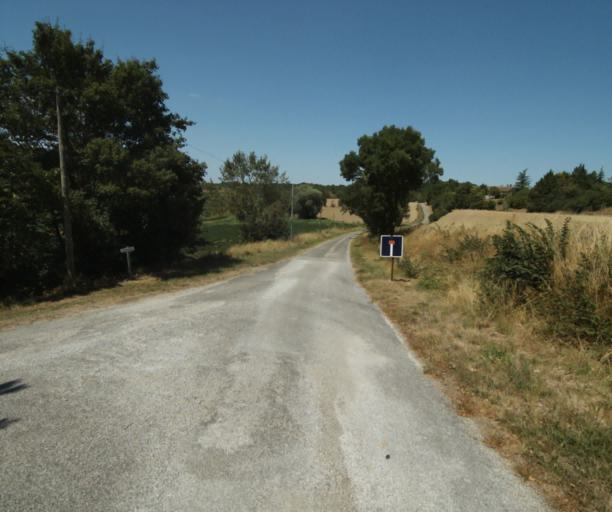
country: FR
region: Midi-Pyrenees
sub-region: Departement de la Haute-Garonne
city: Saint-Felix-Lauragais
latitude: 43.4808
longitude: 1.8572
